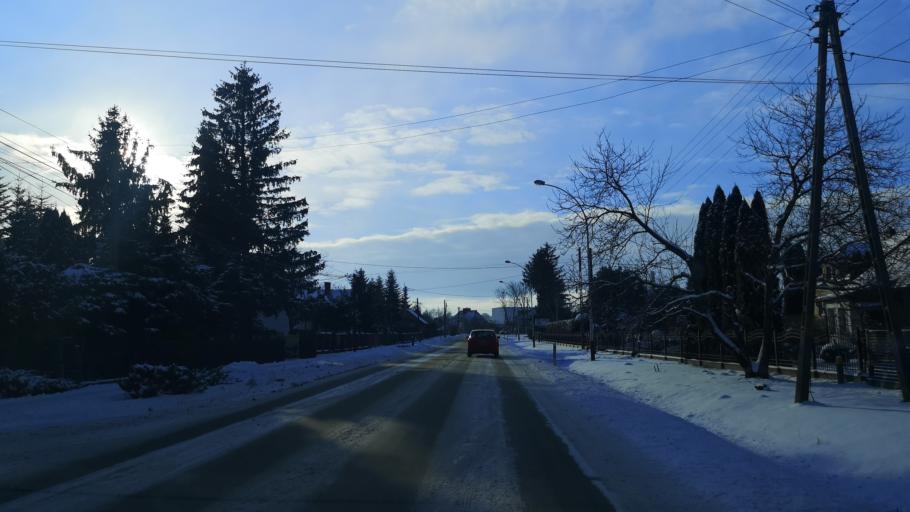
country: PL
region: Subcarpathian Voivodeship
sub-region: Powiat przeworski
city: Przeworsk
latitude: 50.0758
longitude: 22.4936
